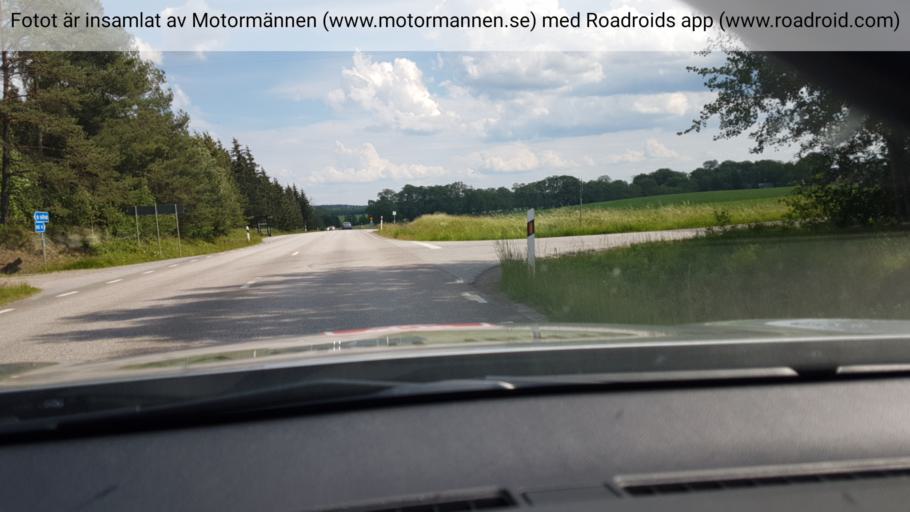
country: SE
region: Vaestra Goetaland
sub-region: Tibro Kommun
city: Tibro
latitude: 58.3478
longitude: 14.1108
